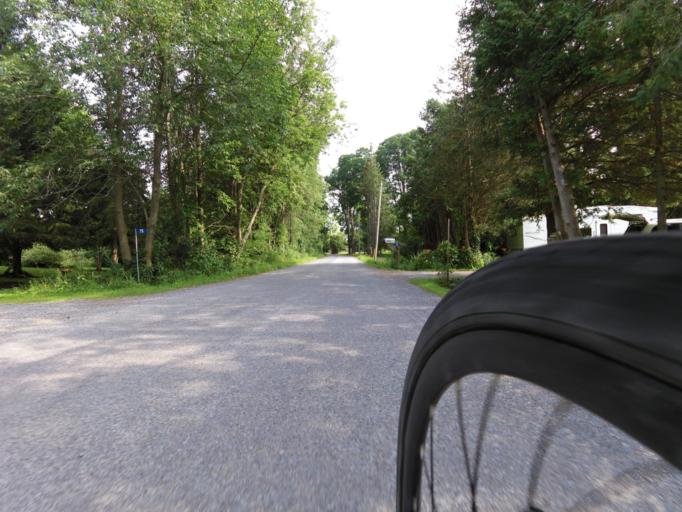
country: CA
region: Ontario
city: Quinte West
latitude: 44.0504
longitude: -77.6302
